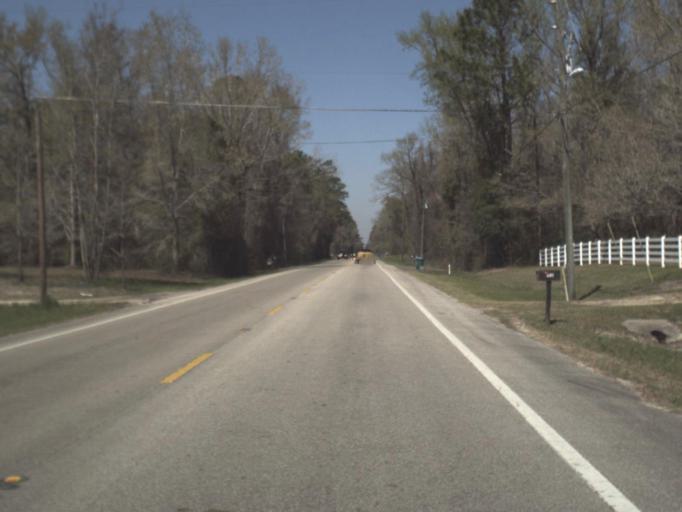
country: US
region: Florida
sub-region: Leon County
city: Woodville
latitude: 30.2526
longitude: -84.2343
